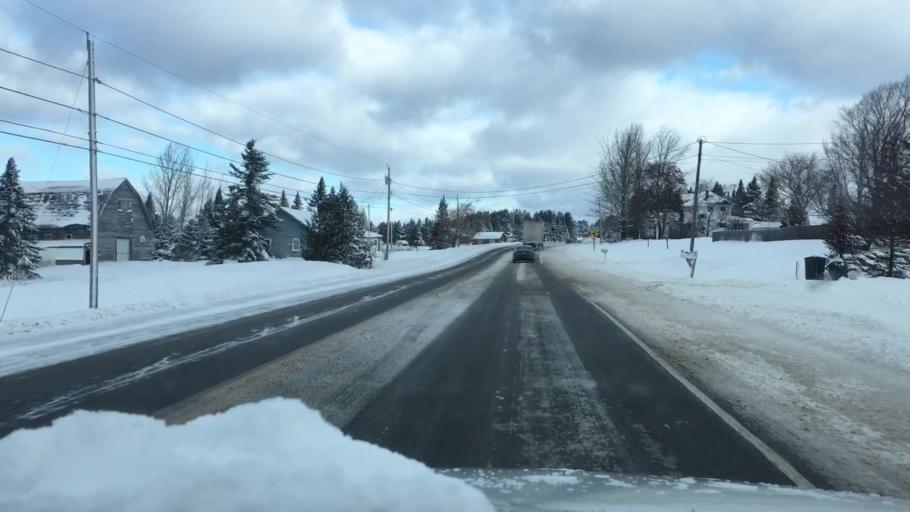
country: US
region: Maine
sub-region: Aroostook County
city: Caribou
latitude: 46.7894
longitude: -67.9904
